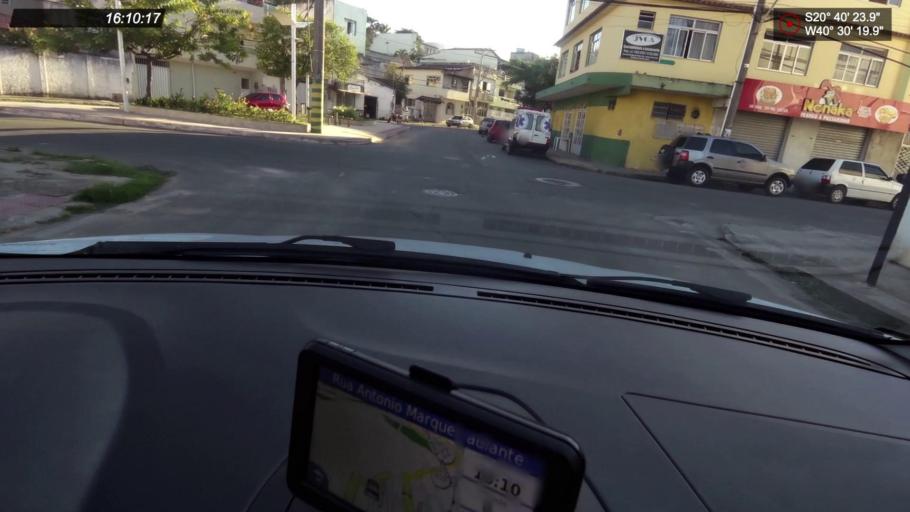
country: BR
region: Espirito Santo
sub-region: Guarapari
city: Guarapari
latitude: -20.6733
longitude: -40.5055
